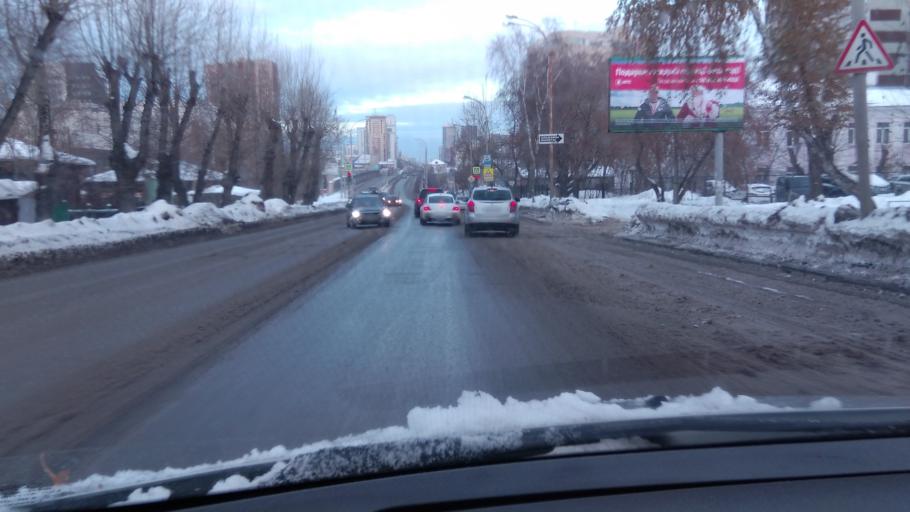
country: RU
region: Sverdlovsk
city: Yekaterinburg
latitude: 56.8106
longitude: 60.5910
